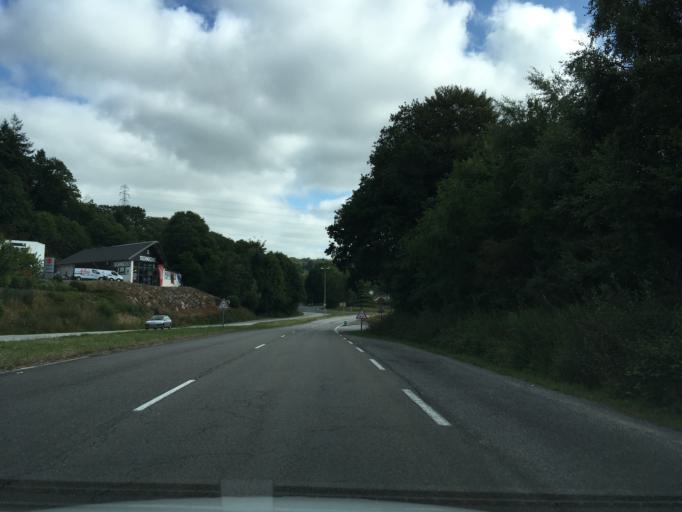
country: FR
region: Brittany
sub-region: Departement du Finistere
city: Quimper
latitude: 48.0173
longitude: -4.0856
